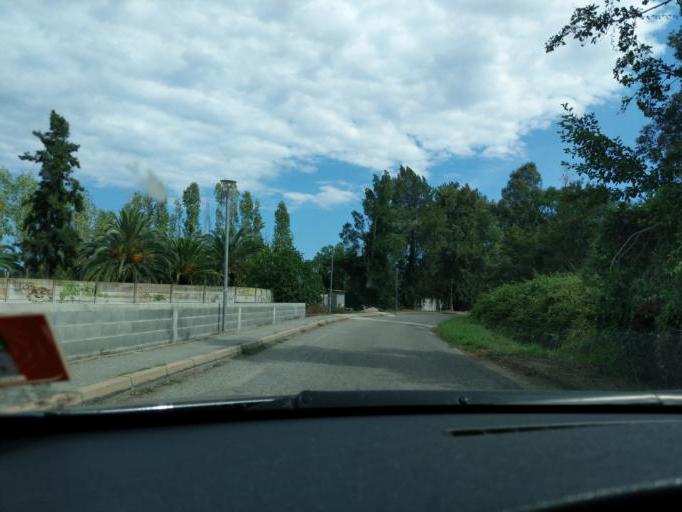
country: FR
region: Corsica
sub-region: Departement de la Haute-Corse
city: Ghisonaccia
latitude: 42.0017
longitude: 9.4431
